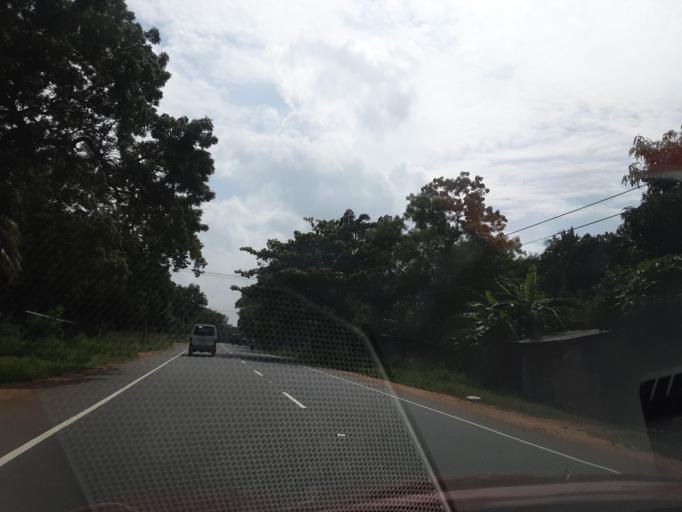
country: LK
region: North Central
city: Anuradhapura
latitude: 8.4957
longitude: 80.5122
